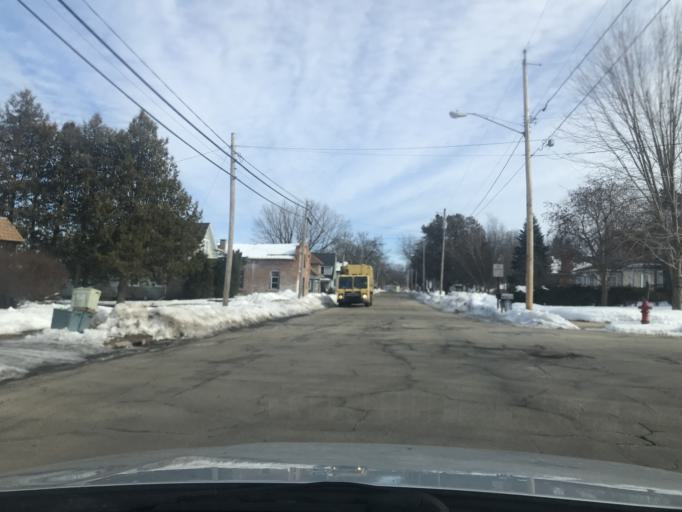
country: US
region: Wisconsin
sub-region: Oconto County
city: Gillett
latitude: 44.8894
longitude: -88.3069
